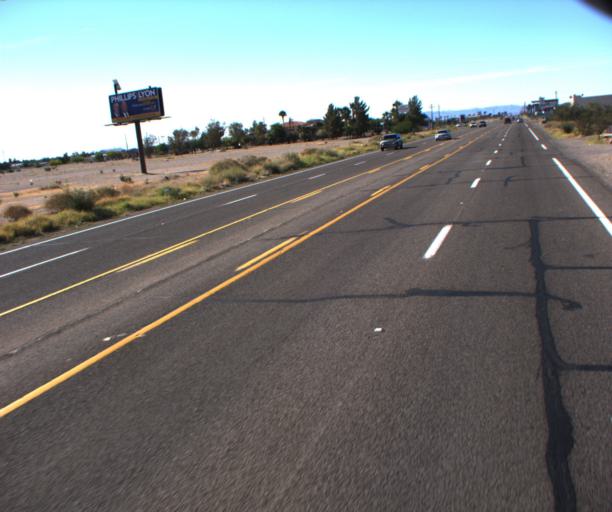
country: US
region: Arizona
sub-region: Mohave County
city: Mohave Valley
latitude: 35.0067
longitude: -114.5981
